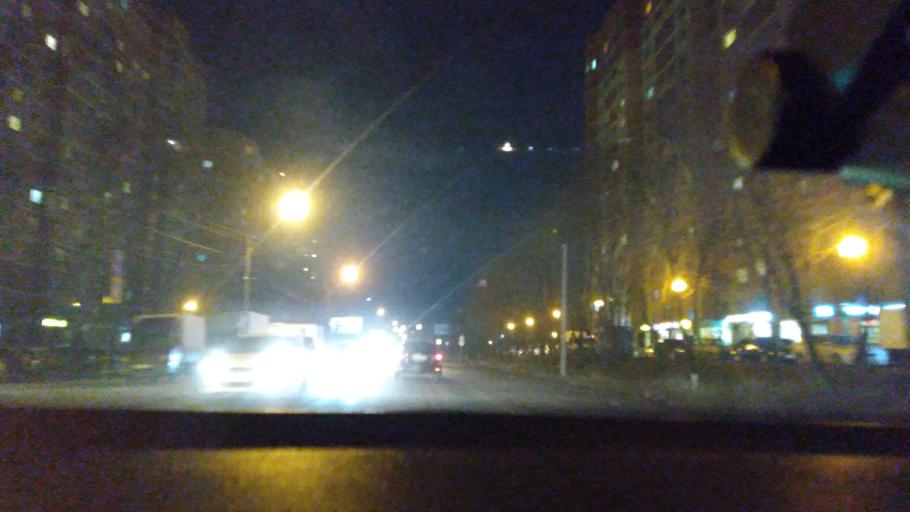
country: RU
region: Moskovskaya
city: Shchelkovo
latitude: 55.9387
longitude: 37.9733
